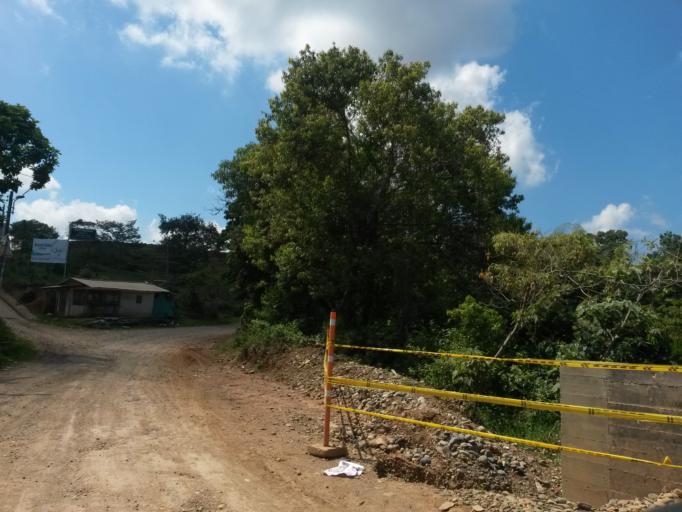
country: CO
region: Cauca
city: Buenos Aires
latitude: 3.0187
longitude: -76.6442
